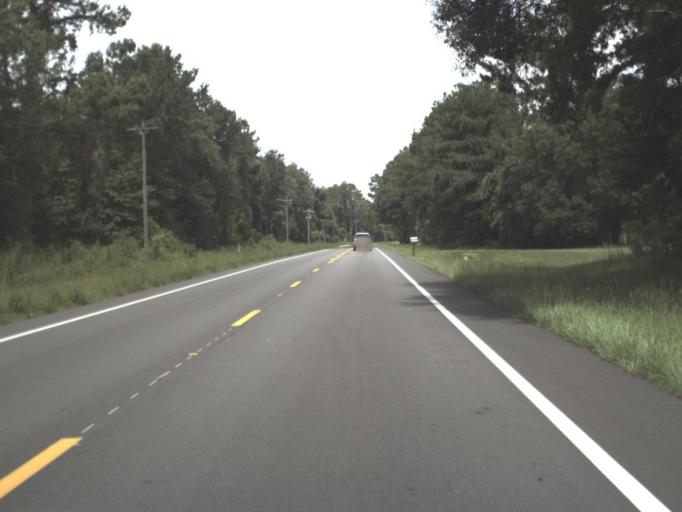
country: US
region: Florida
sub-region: Jefferson County
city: Monticello
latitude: 30.4845
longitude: -83.6962
